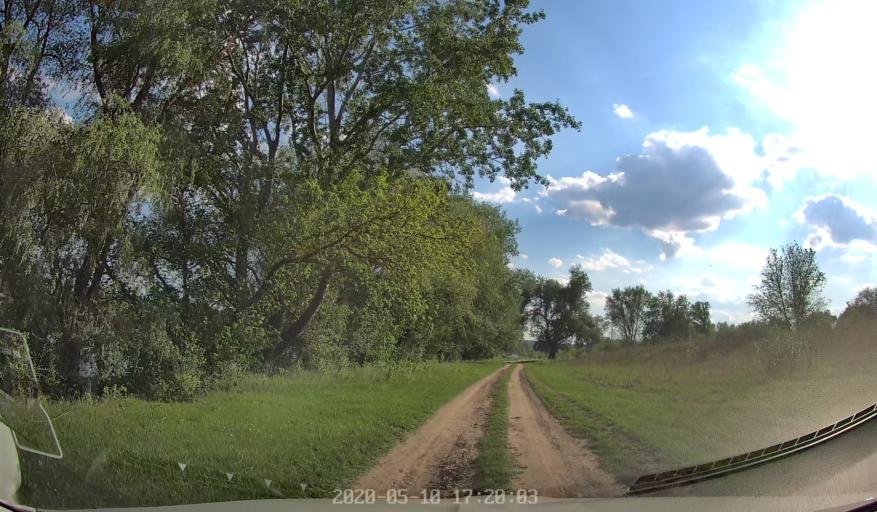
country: MD
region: Chisinau
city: Vadul lui Voda
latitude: 47.1288
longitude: 29.0877
